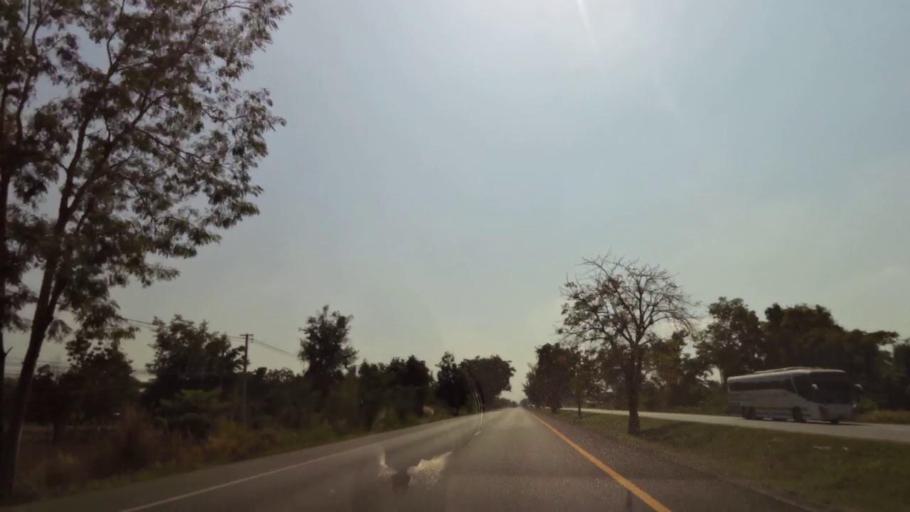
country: TH
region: Phichit
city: Bueng Na Rang
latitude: 16.2801
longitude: 100.1273
